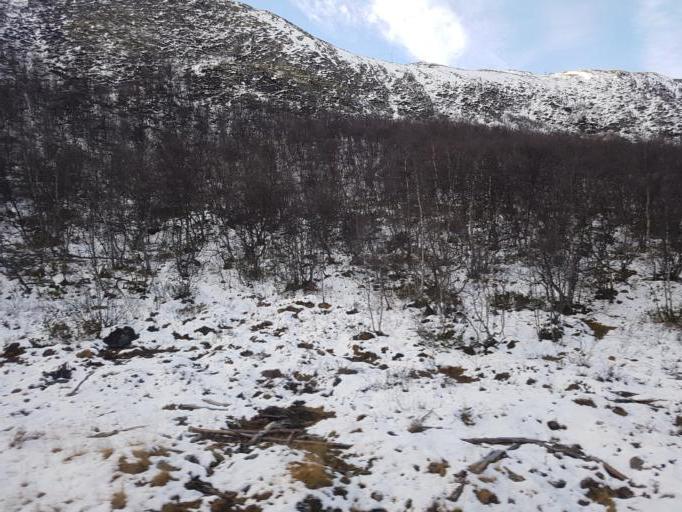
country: NO
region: Oppland
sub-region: Dovre
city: Dovre
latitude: 62.2172
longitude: 9.5479
